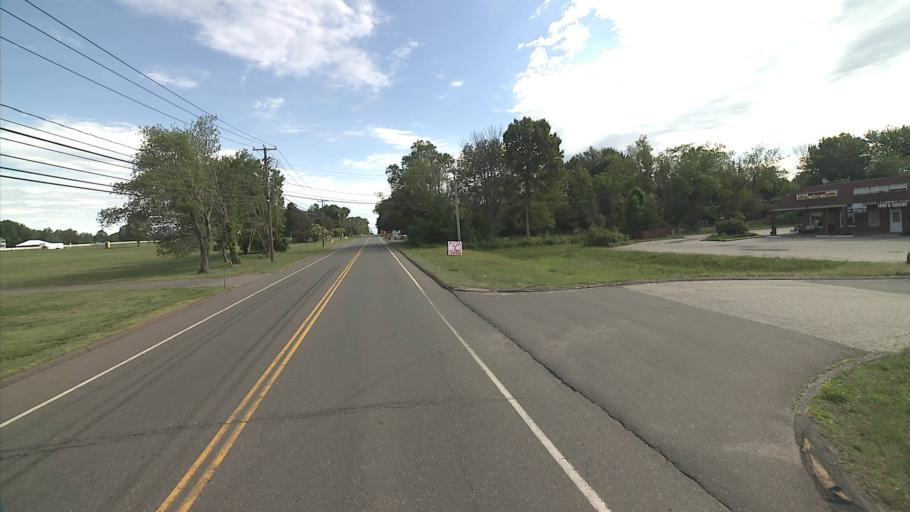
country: US
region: Connecticut
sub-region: New Haven County
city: Prospect
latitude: 41.4374
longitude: -72.9918
